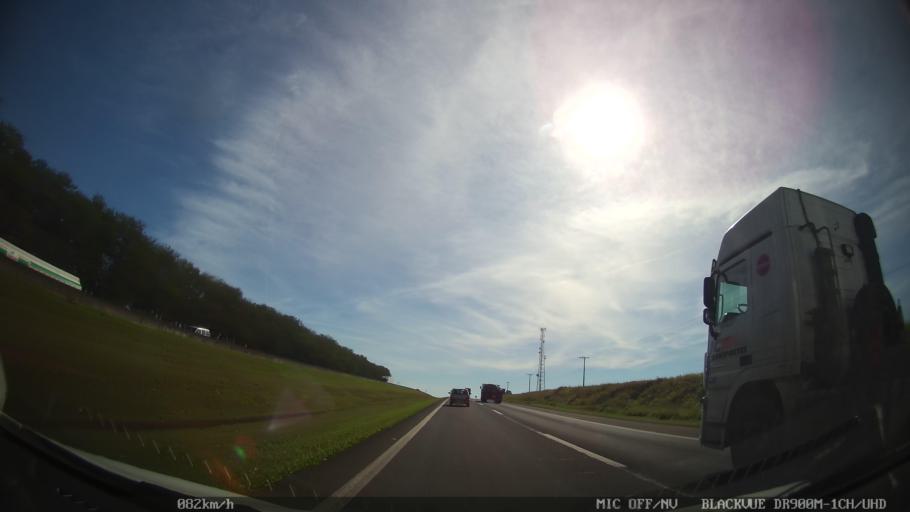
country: BR
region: Sao Paulo
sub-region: Leme
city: Leme
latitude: -22.2656
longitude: -47.3910
